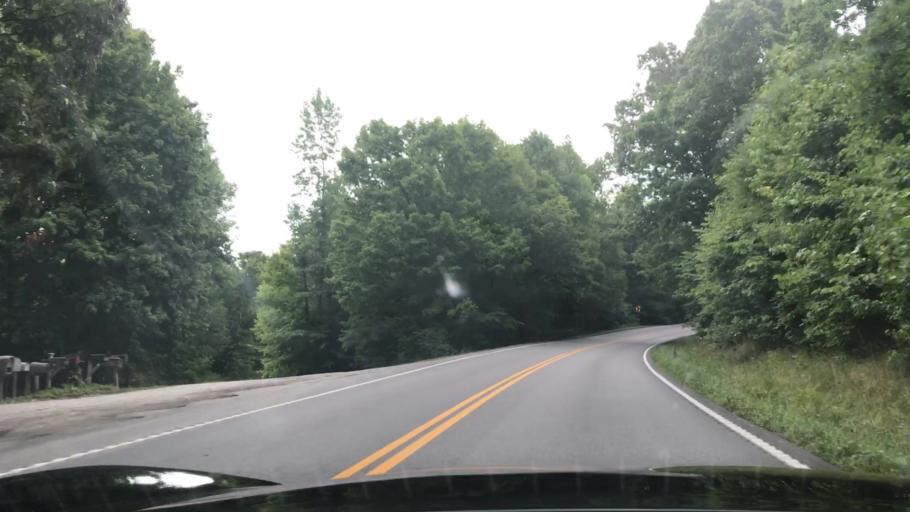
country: US
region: Kentucky
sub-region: Muhlenberg County
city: Central City
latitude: 37.2054
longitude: -87.0384
